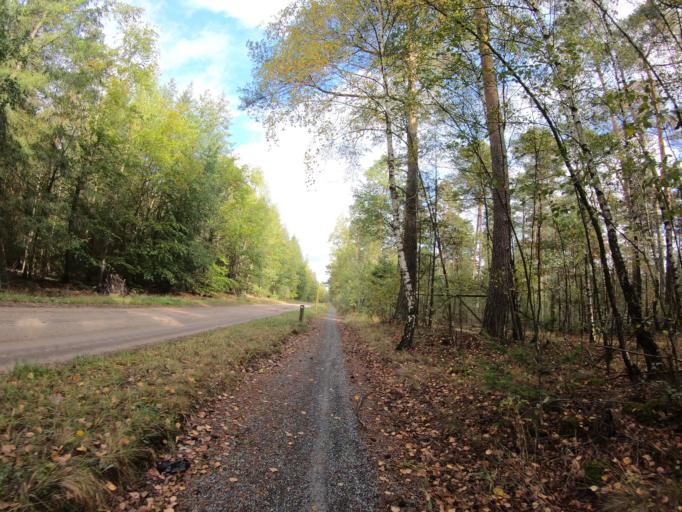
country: DE
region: Lower Saxony
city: Wesendorf
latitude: 52.5716
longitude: 10.5656
